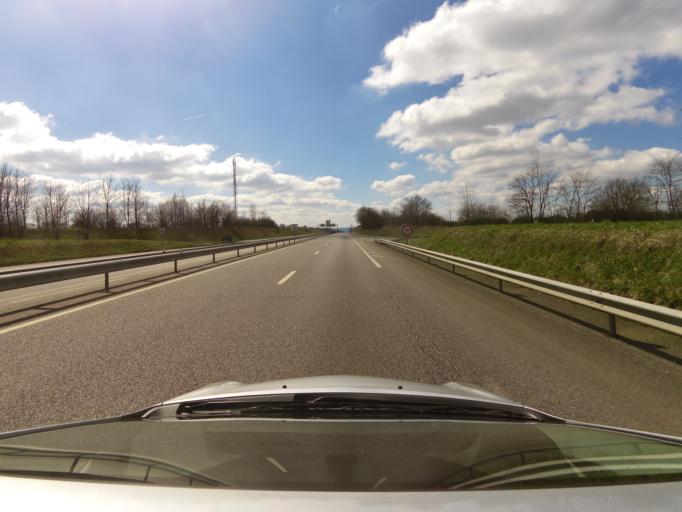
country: FR
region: Haute-Normandie
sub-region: Departement de la Seine-Maritime
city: Neufchatel-en-Bray
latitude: 49.7428
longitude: 1.4732
